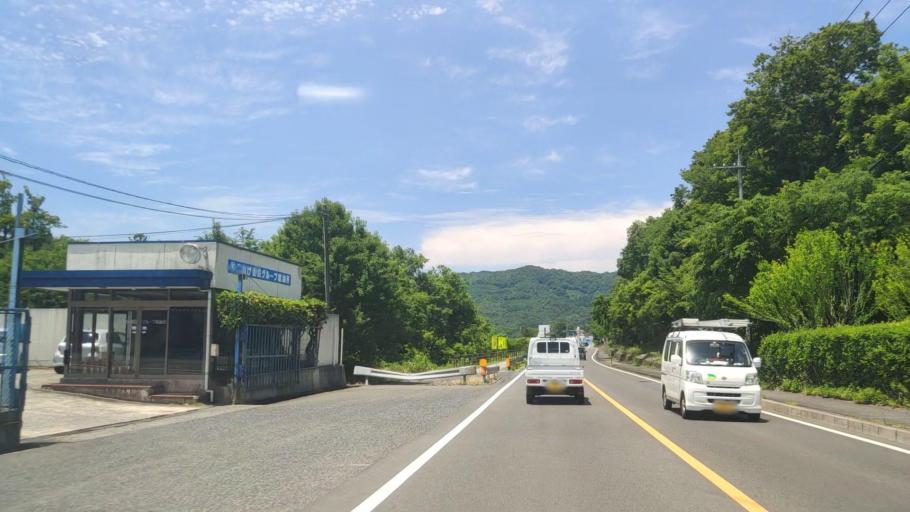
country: JP
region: Tottori
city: Tottori
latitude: 35.4045
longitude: 134.2576
